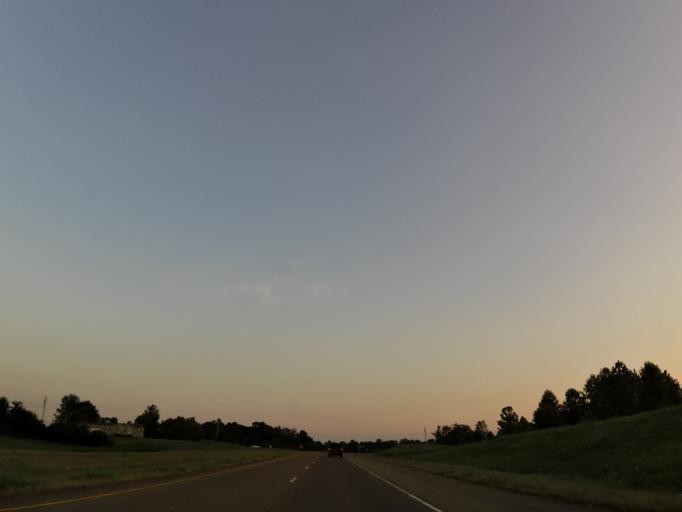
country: US
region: Tennessee
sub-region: Henry County
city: Paris
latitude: 36.2013
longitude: -88.4080
